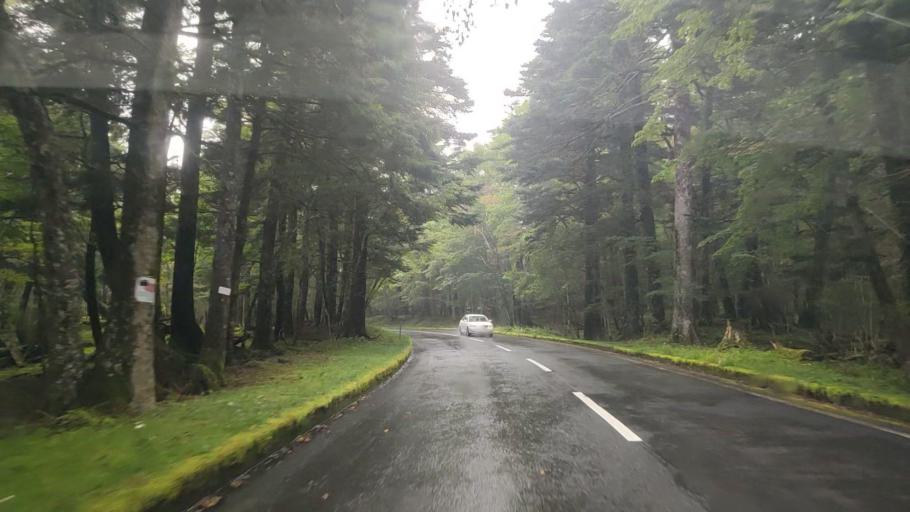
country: JP
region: Shizuoka
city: Fujinomiya
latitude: 35.3192
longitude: 138.7235
